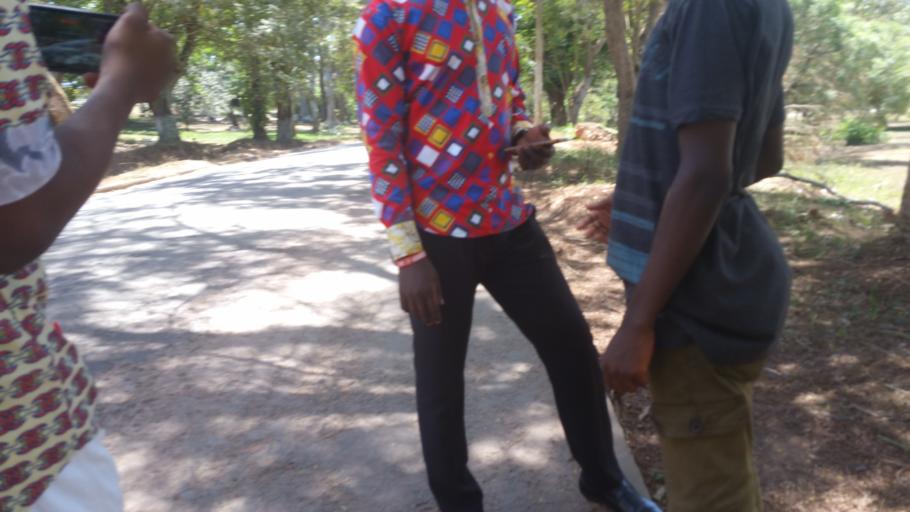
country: GH
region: Central
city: Cape Coast
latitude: 5.1170
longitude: -1.2857
